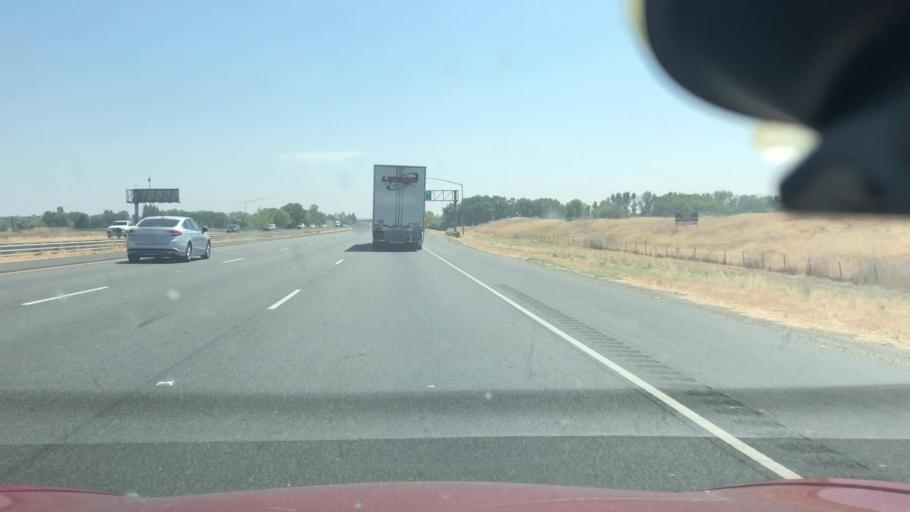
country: US
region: California
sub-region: Sacramento County
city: Parkway
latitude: 38.4368
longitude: -121.4898
